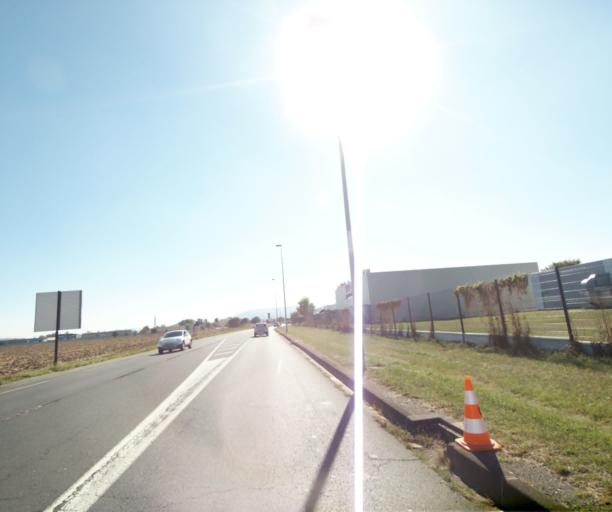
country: FR
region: Auvergne
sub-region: Departement du Puy-de-Dome
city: Gerzat
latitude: 45.8014
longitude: 3.1317
